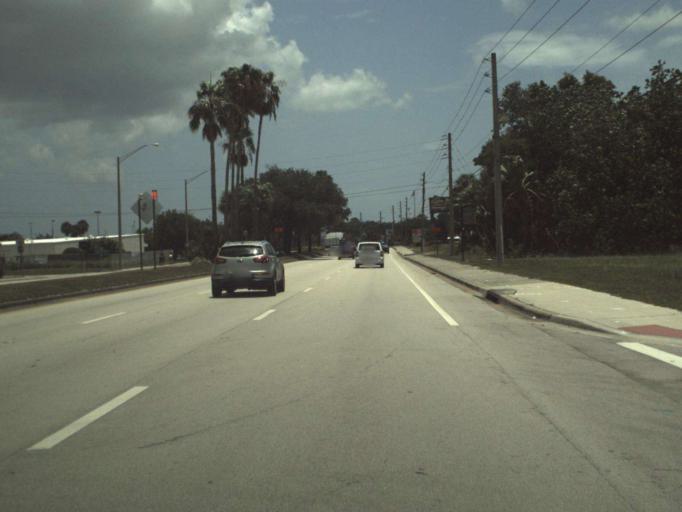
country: US
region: Florida
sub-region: Saint Lucie County
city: Fort Pierce South
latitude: 27.4184
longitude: -80.3801
